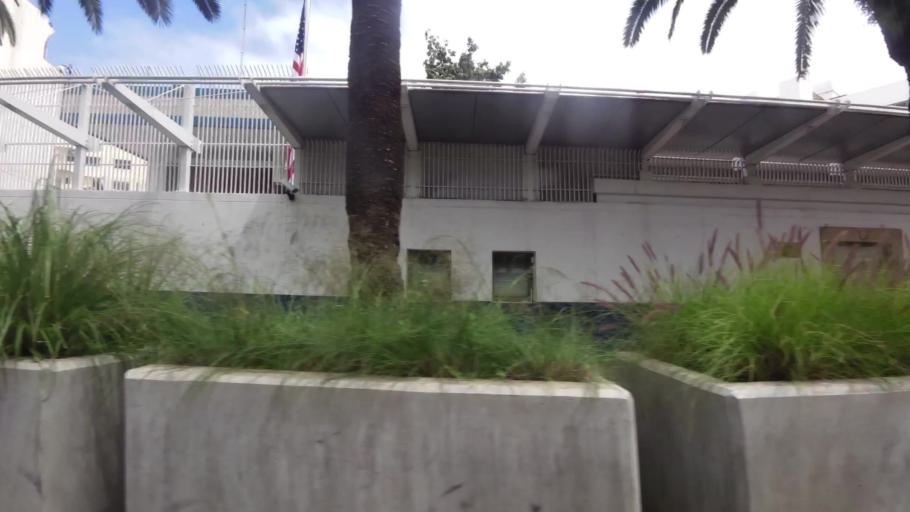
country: MA
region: Grand Casablanca
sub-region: Casablanca
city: Casablanca
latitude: 33.5909
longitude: -7.6270
